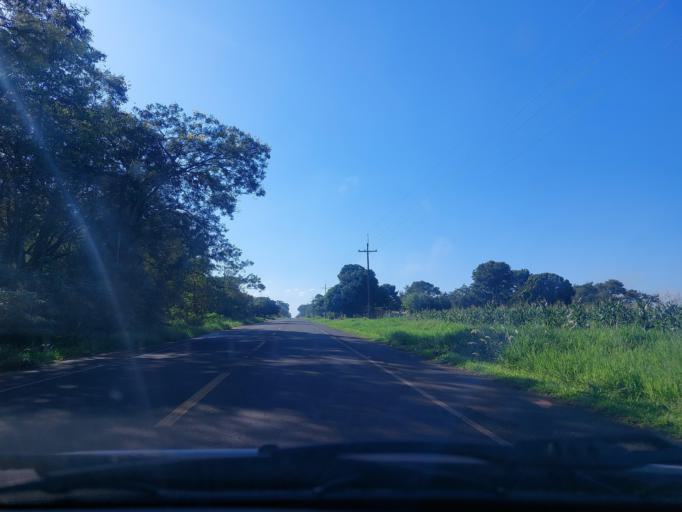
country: PY
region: San Pedro
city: Guayaybi
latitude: -24.5320
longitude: -56.5051
